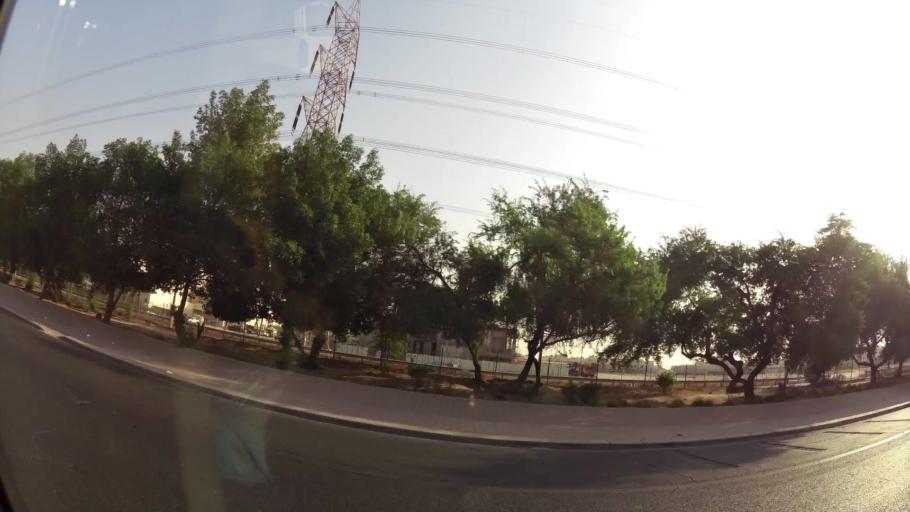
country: KW
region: Muhafazat Hawalli
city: Hawalli
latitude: 29.3058
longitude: 48.0076
